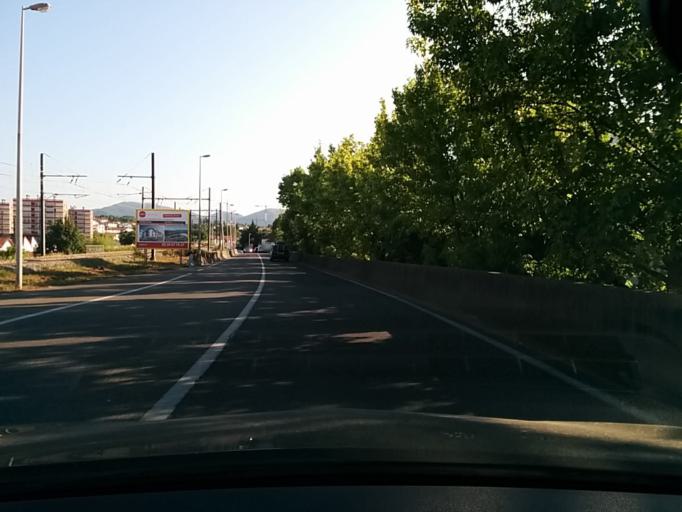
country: FR
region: Aquitaine
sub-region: Departement des Pyrenees-Atlantiques
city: Saint-Jean-de-Luz
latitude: 43.3839
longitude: -1.6662
